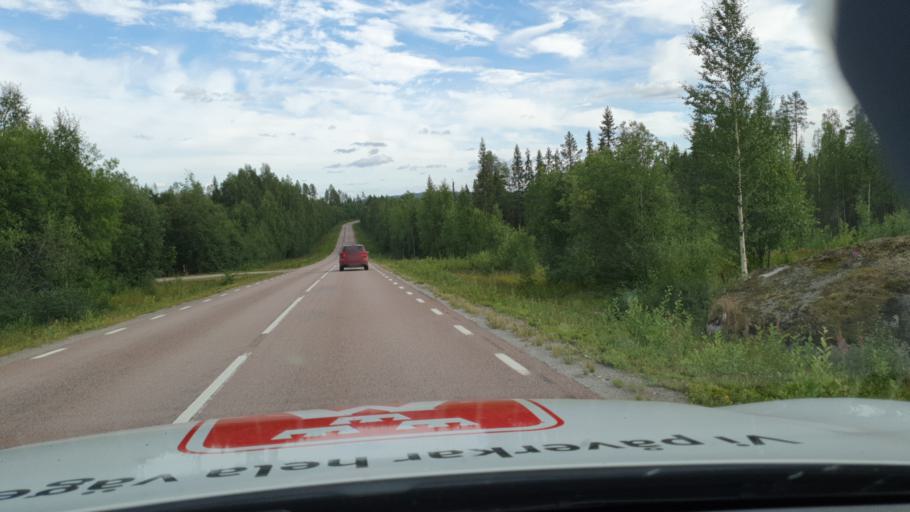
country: SE
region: Vaesternorrland
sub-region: Solleftea Kommun
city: As
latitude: 63.6173
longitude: 16.0944
